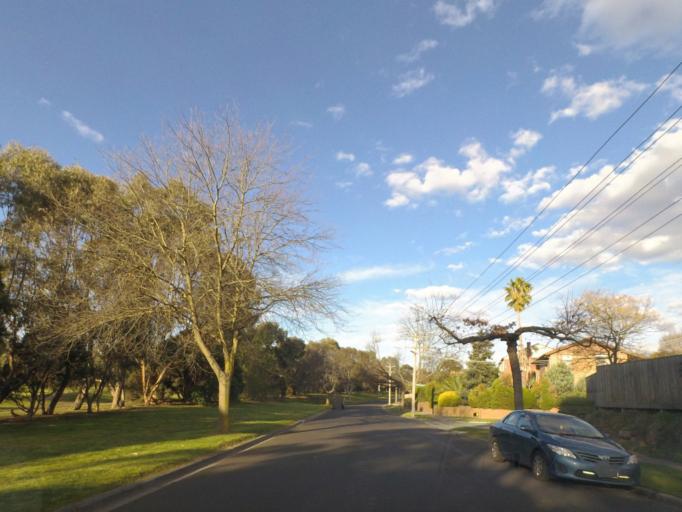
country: AU
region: Victoria
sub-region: Boroondara
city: Balwyn North
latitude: -37.7814
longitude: 145.0912
